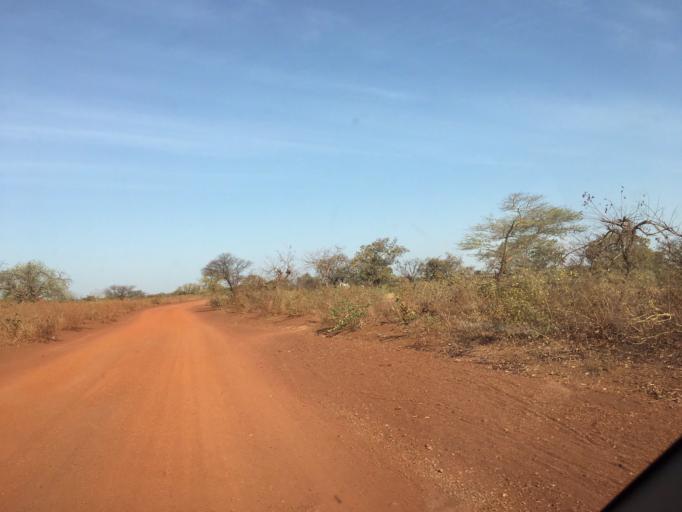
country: BF
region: Plateau-Central
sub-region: Province du Kourweogo
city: Bousse
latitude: 12.5637
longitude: -1.9055
